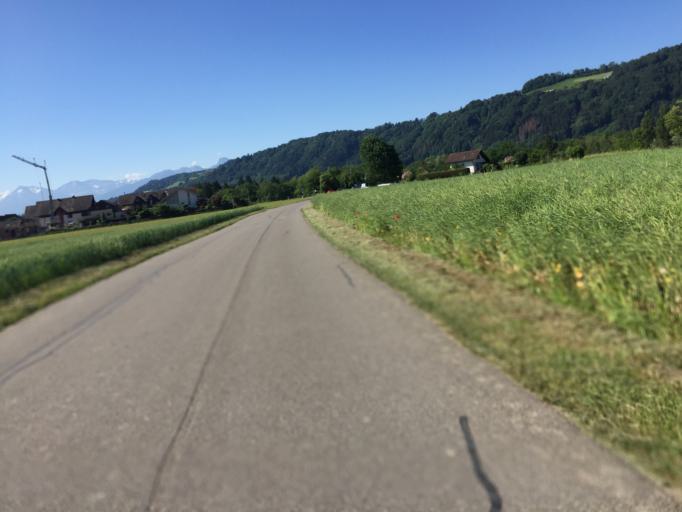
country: CH
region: Bern
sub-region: Bern-Mittelland District
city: Rubigen
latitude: 46.8972
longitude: 7.5387
